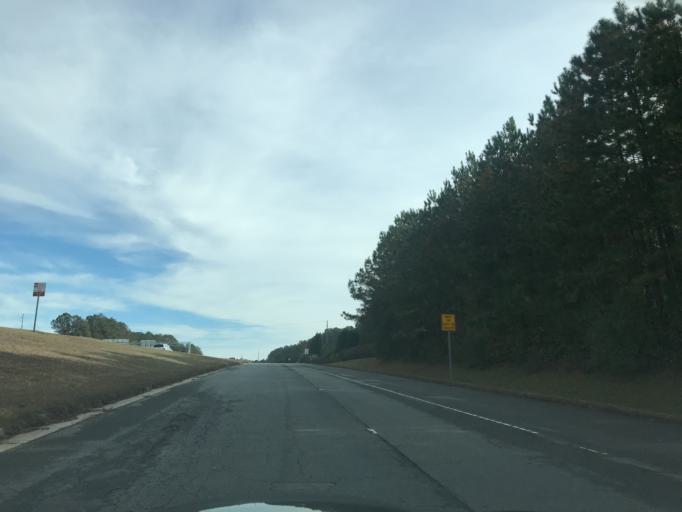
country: US
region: North Carolina
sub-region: Wake County
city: Cary
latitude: 35.8065
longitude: -78.7219
